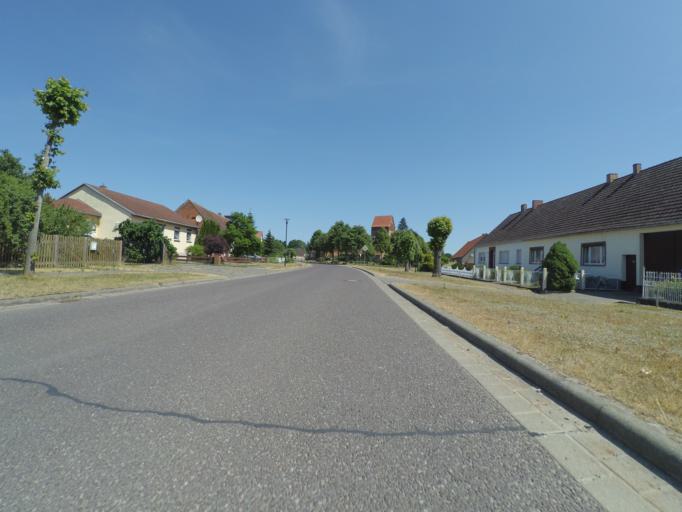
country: DE
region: Brandenburg
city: Heiligengrabe
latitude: 53.2023
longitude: 12.3354
